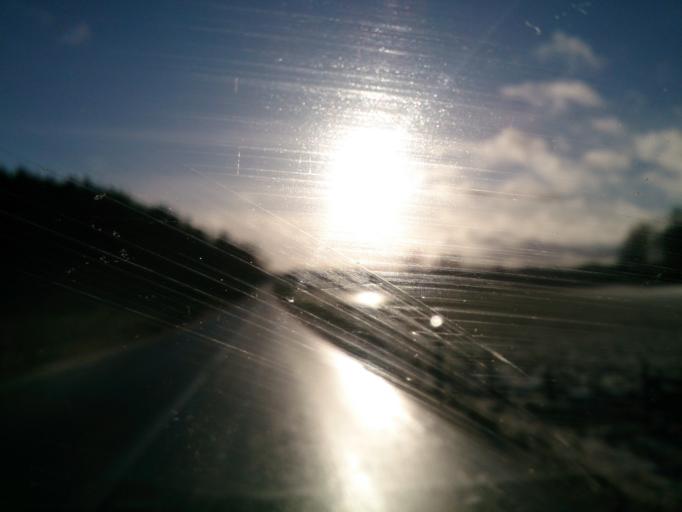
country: SE
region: OEstergoetland
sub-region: Atvidabergs Kommun
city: Atvidaberg
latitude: 58.2973
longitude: 15.8909
